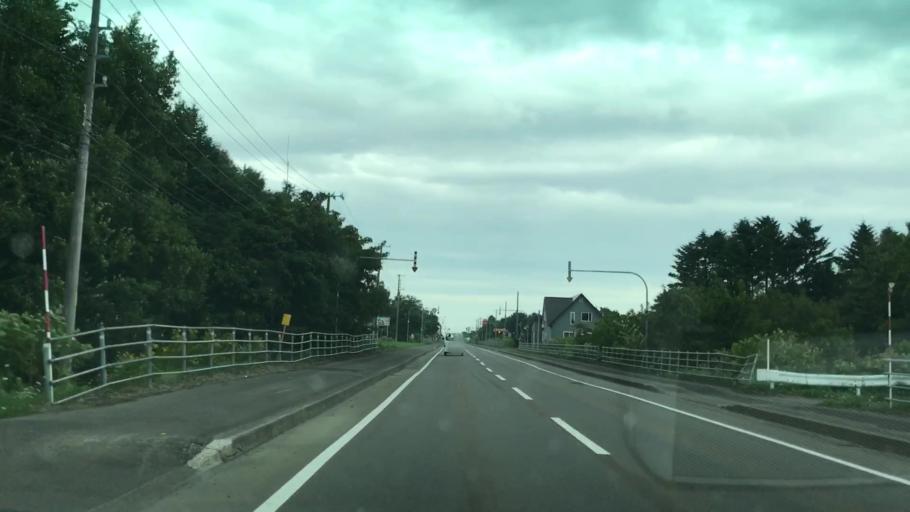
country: JP
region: Hokkaido
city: Iwanai
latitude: 42.7830
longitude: 140.2364
